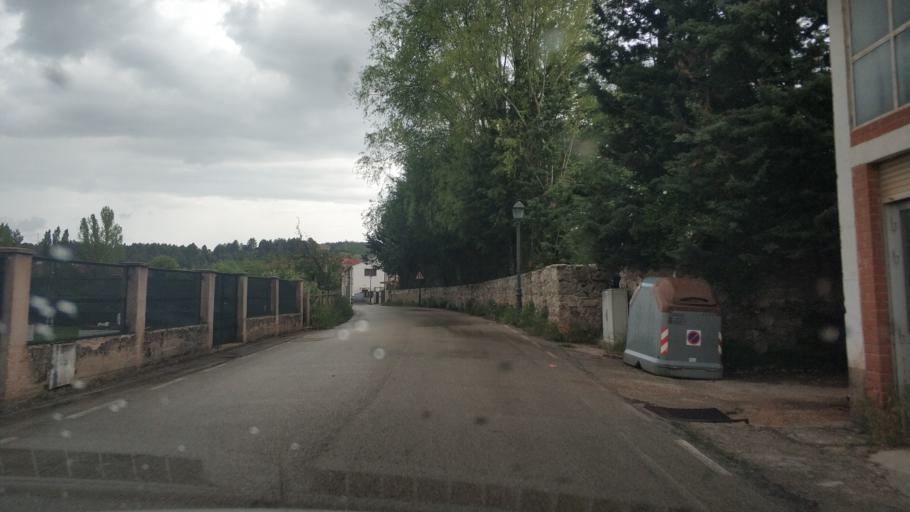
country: ES
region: Castille and Leon
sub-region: Provincia de Soria
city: San Leonardo de Yague
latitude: 41.8324
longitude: -3.0672
